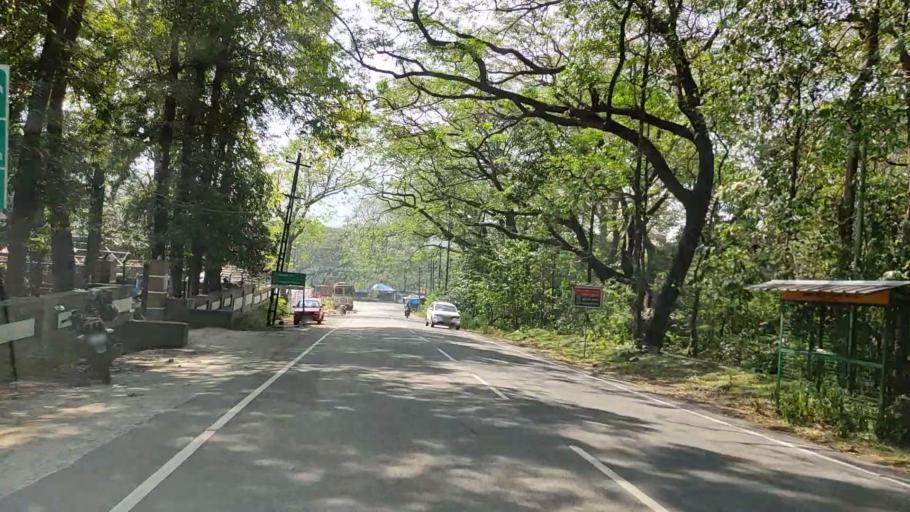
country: IN
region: Kerala
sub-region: Kollam
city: Punalur
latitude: 8.9585
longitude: 77.0657
